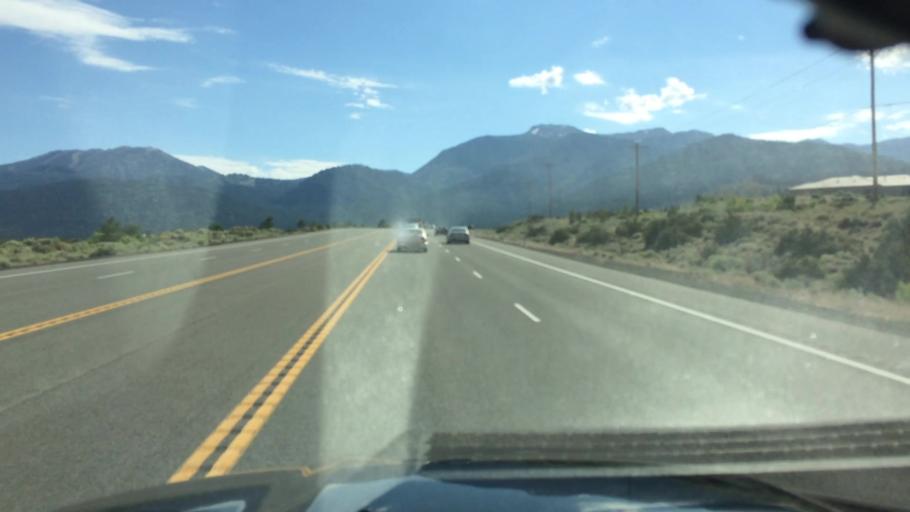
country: US
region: Nevada
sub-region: Washoe County
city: Reno
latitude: 39.3810
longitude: -119.8229
